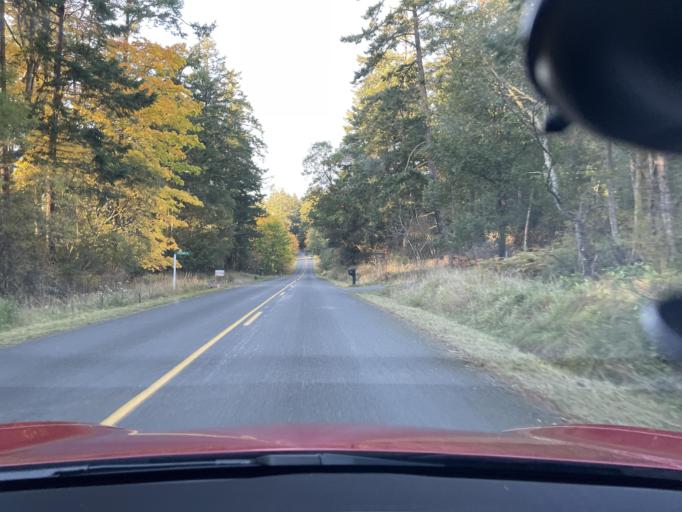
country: US
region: Washington
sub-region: San Juan County
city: Friday Harbor
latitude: 48.5471
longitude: -123.1589
